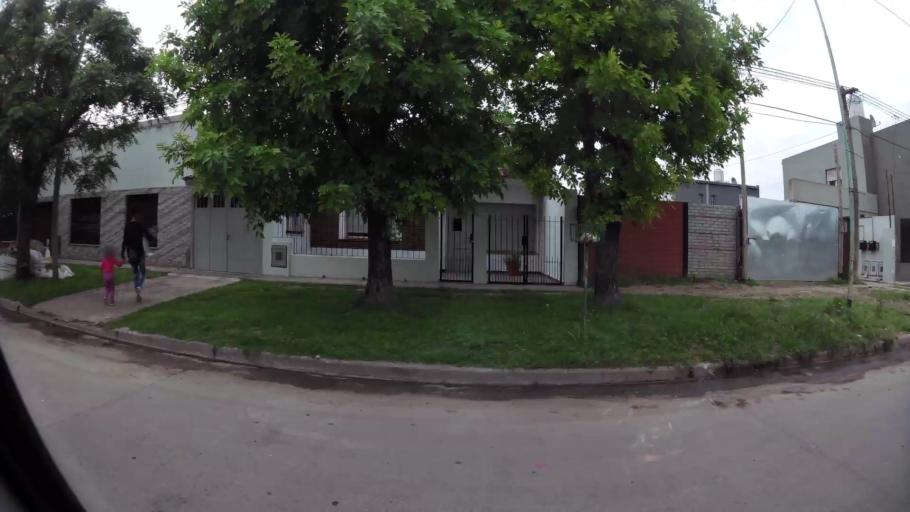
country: AR
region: Buenos Aires
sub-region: Partido de La Plata
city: La Plata
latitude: -34.9138
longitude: -57.9957
